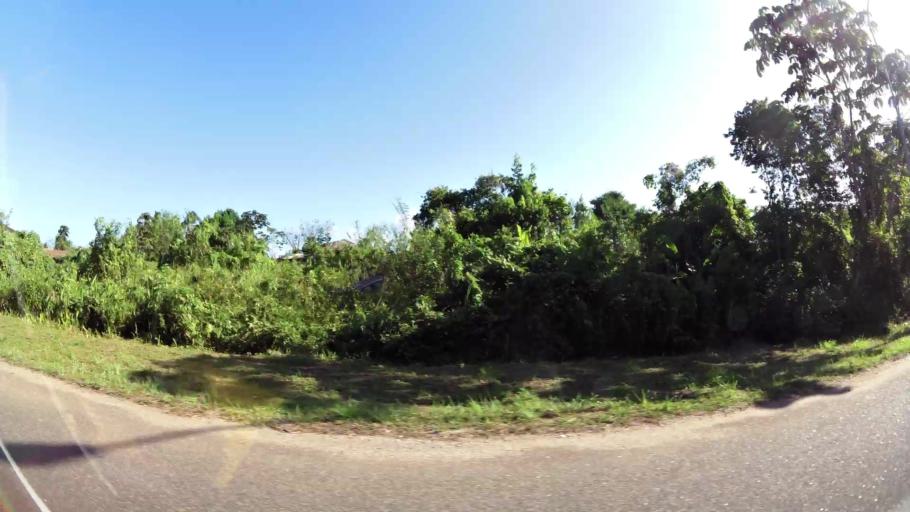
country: GF
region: Guyane
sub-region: Guyane
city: Matoury
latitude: 4.8597
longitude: -52.2730
